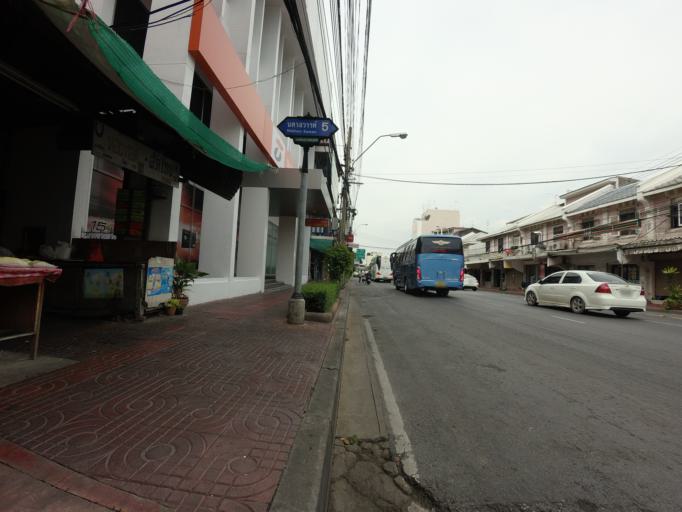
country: TH
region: Bangkok
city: Pom Prap Sattru Phai
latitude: 13.7593
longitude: 100.5111
